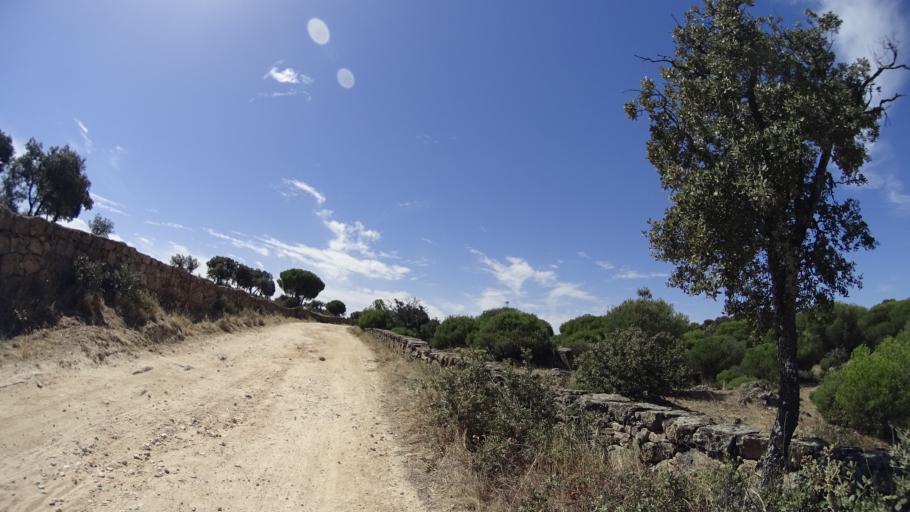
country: ES
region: Madrid
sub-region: Provincia de Madrid
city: Torrelodones
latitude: 40.5662
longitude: -3.9386
